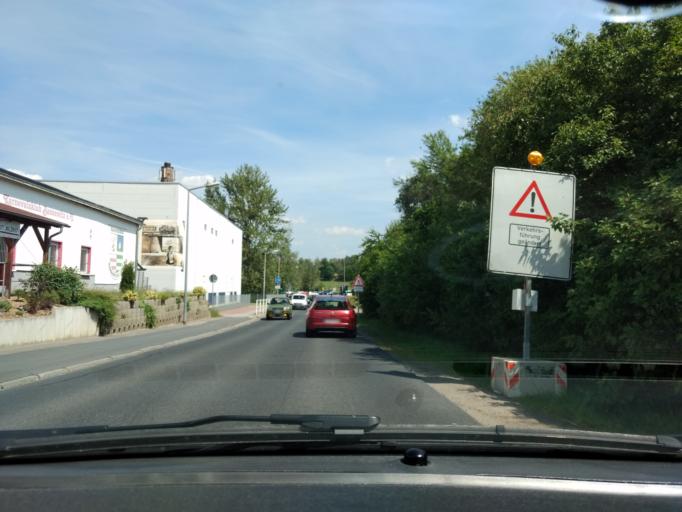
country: DE
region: Saxony
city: Bannewitz
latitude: 50.9893
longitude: 13.7104
